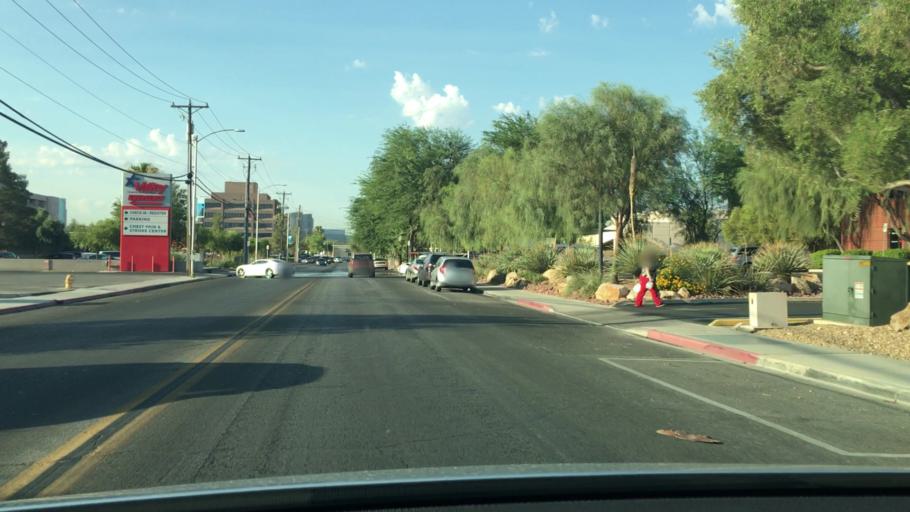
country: US
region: Nevada
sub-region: Clark County
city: Las Vegas
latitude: 36.1632
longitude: -115.1700
